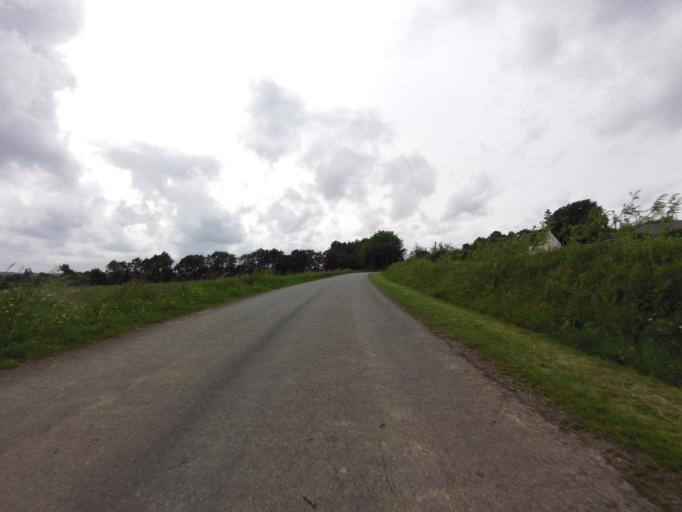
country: FR
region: Brittany
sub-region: Departement du Morbihan
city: Molac
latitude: 47.7333
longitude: -2.4595
